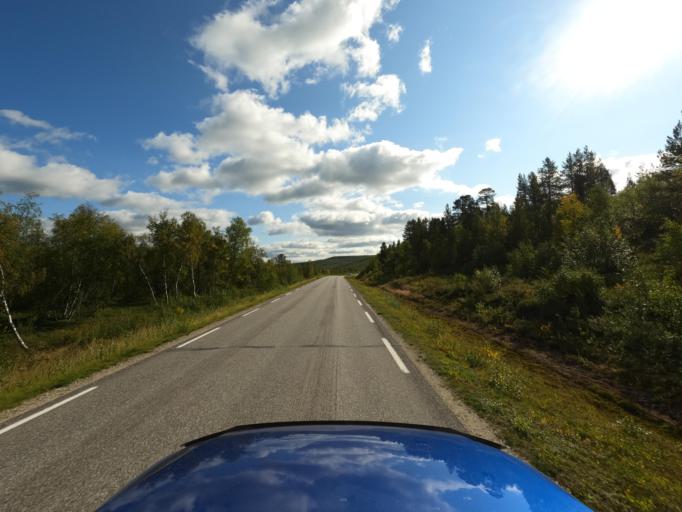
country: NO
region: Finnmark Fylke
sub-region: Karasjok
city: Karasjohka
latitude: 69.4461
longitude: 25.6236
